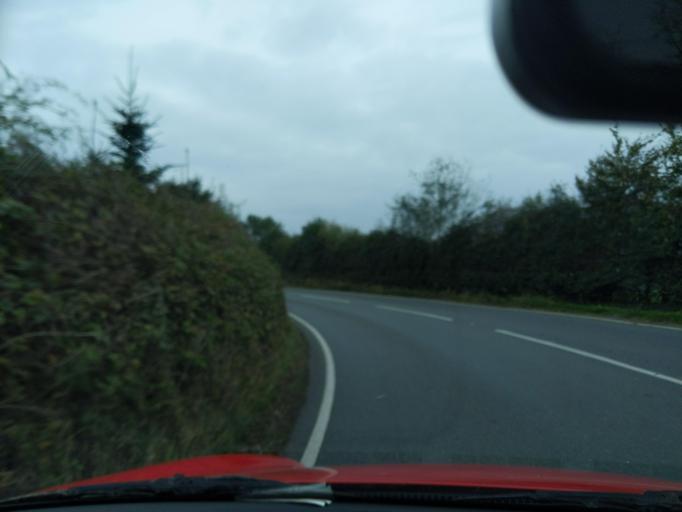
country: GB
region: England
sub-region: Devon
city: Okehampton
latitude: 50.8452
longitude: -4.0691
